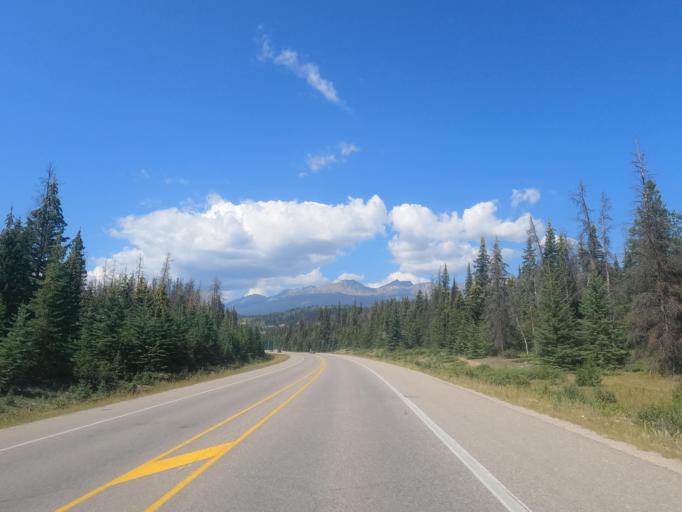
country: CA
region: Alberta
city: Jasper Park Lodge
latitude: 52.8604
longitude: -118.0816
